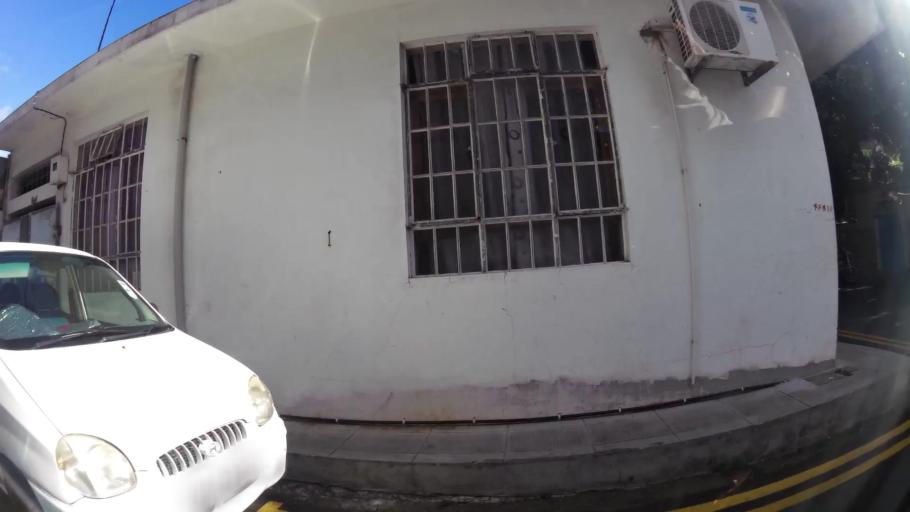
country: MU
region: Port Louis
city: Port Louis
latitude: -20.1560
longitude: 57.5127
